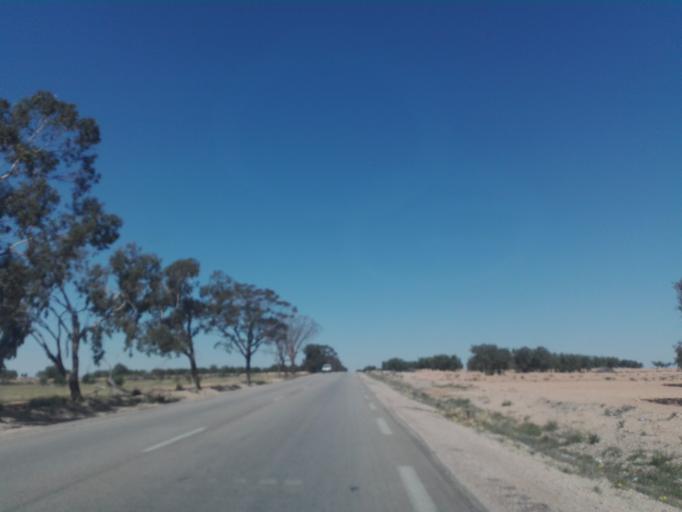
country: TN
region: Safaqis
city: Bi'r `Ali Bin Khalifah
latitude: 34.7512
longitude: 10.3451
